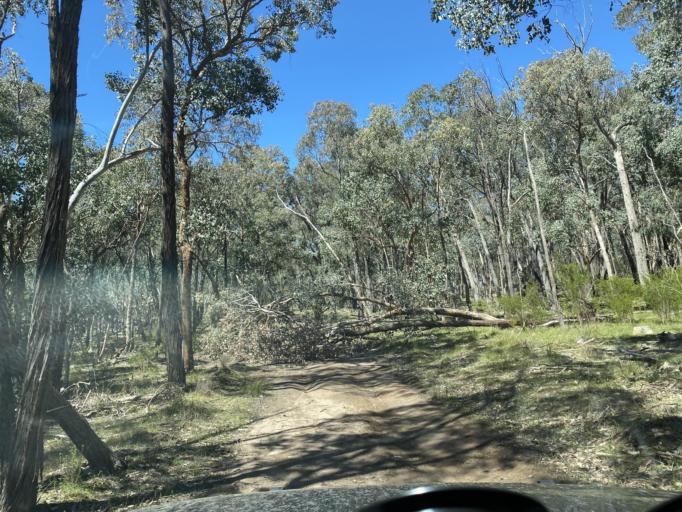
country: AU
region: Victoria
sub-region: Benalla
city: Benalla
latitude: -36.7028
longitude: 146.1522
